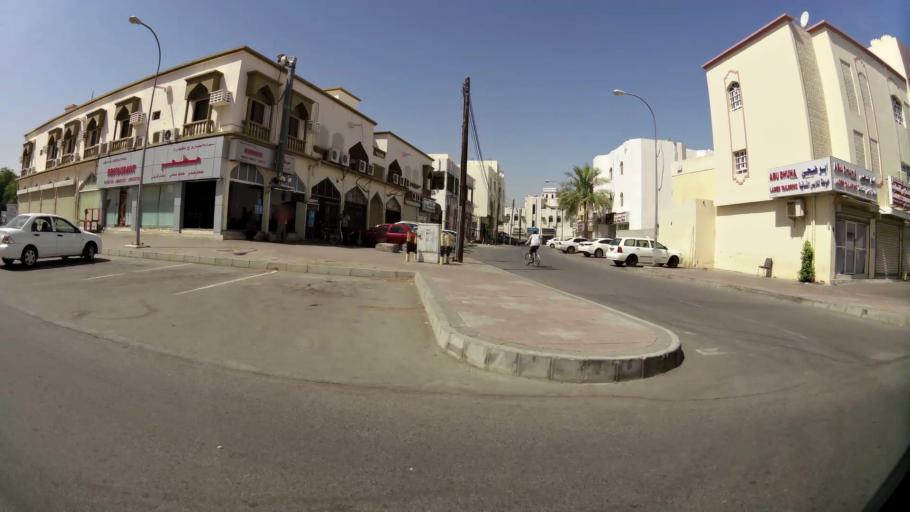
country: OM
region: Muhafazat Masqat
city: Bawshar
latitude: 23.5915
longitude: 58.4062
